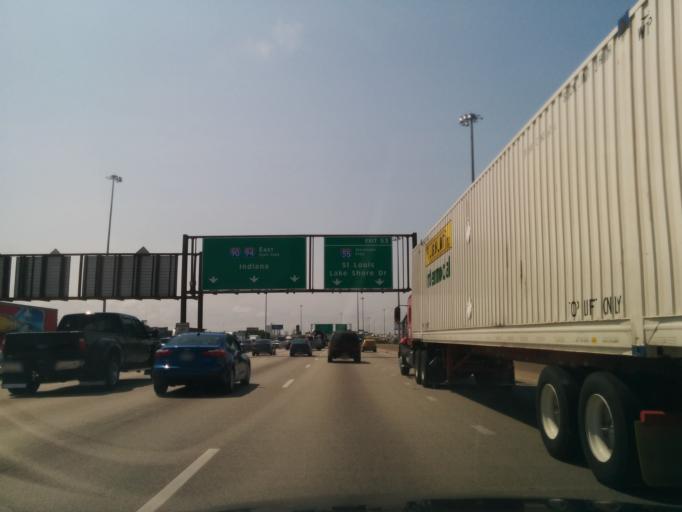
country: US
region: Illinois
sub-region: Cook County
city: Chicago
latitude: 41.8606
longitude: -87.6446
